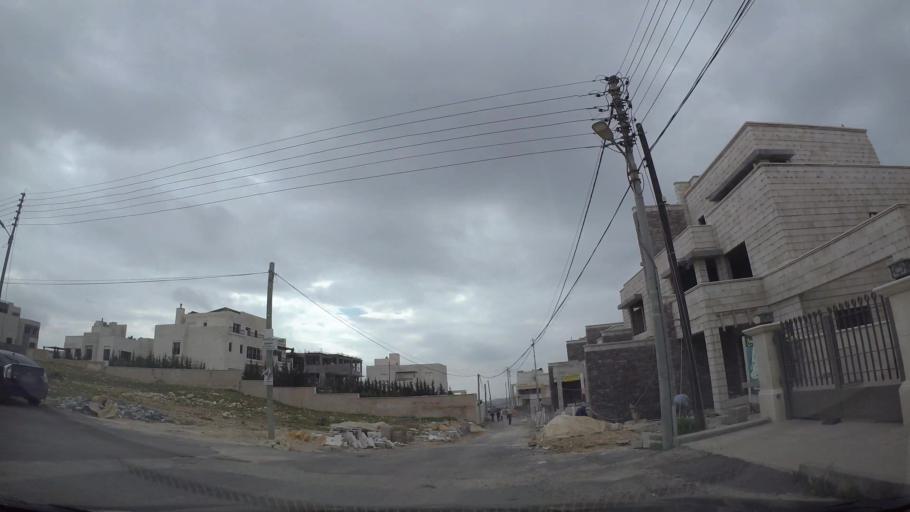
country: JO
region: Amman
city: Wadi as Sir
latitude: 31.9258
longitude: 35.8509
